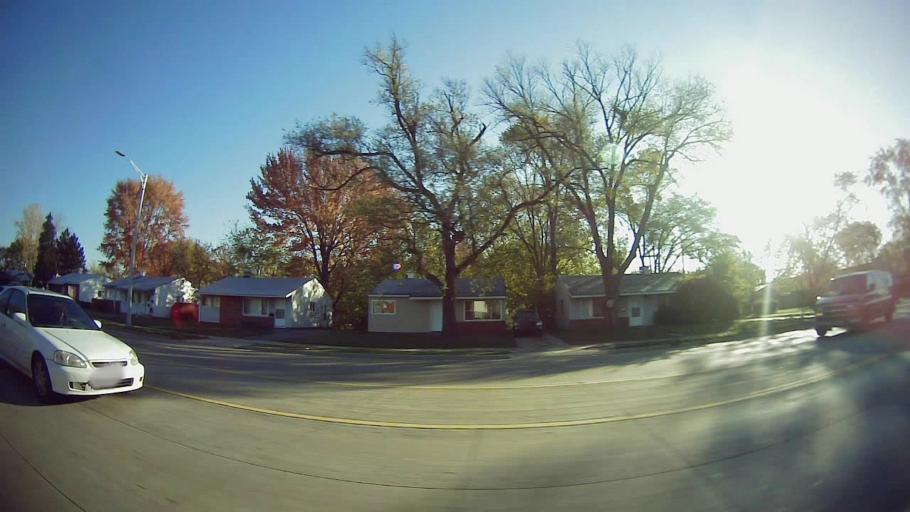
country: US
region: Michigan
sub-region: Oakland County
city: Oak Park
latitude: 42.4575
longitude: -83.1818
